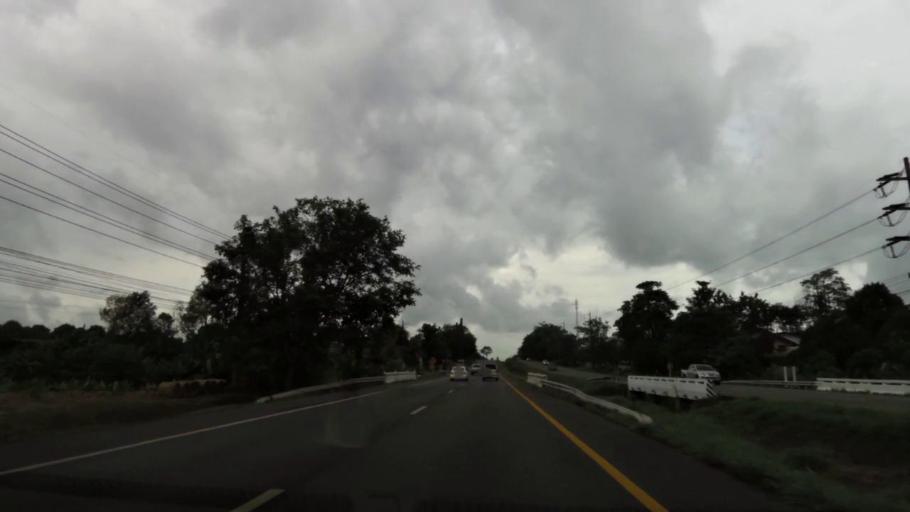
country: TH
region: Chanthaburi
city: Tha Mai
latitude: 12.6840
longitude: 102.0033
